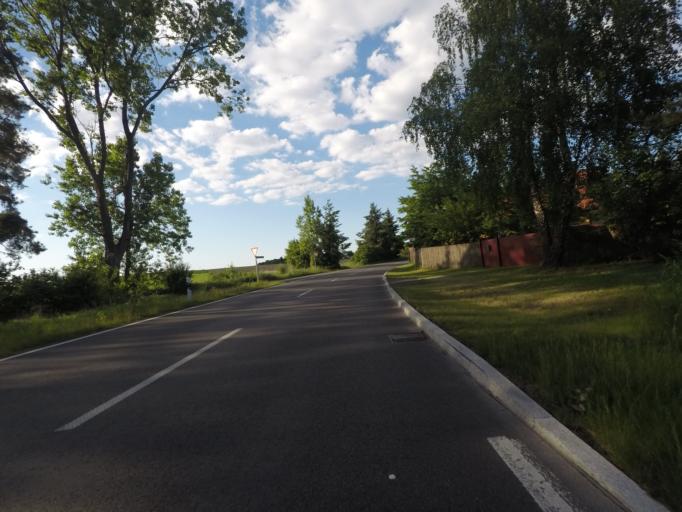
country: DE
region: Brandenburg
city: Britz
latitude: 52.8717
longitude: 13.8079
